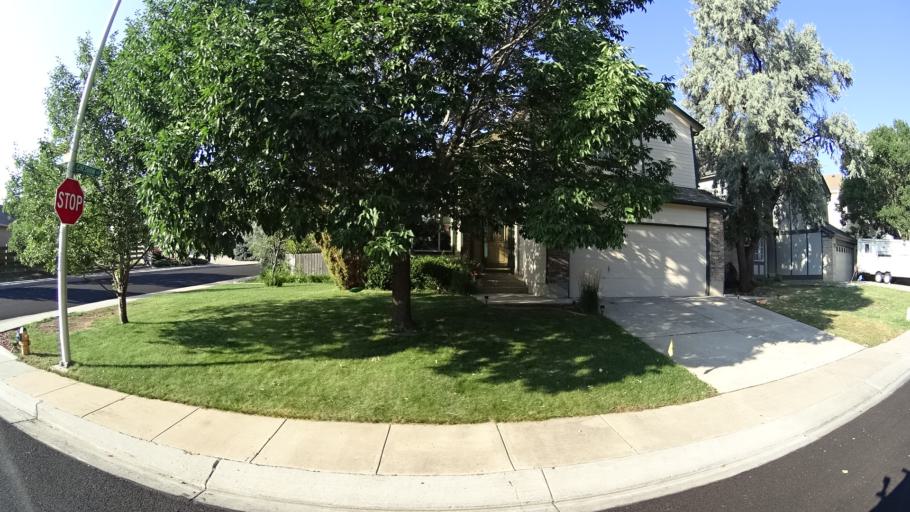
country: US
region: Colorado
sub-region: El Paso County
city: Colorado Springs
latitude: 38.8901
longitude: -104.8515
